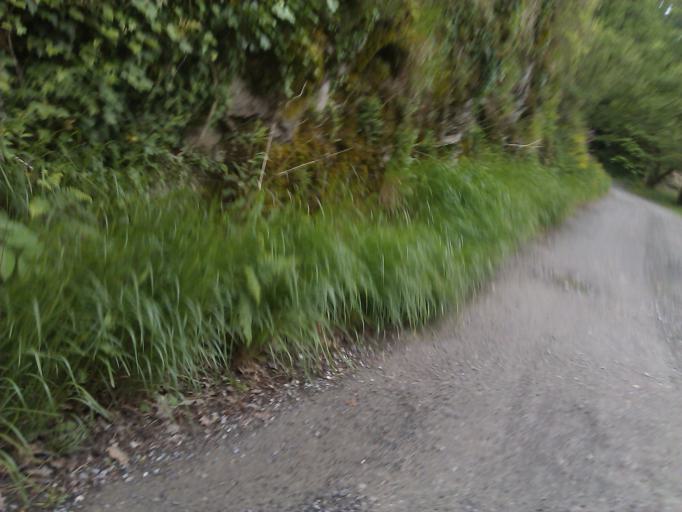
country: ES
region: Basque Country
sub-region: Provincia de Guipuzcoa
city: Elduayen
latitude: 43.1749
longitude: -1.9812
